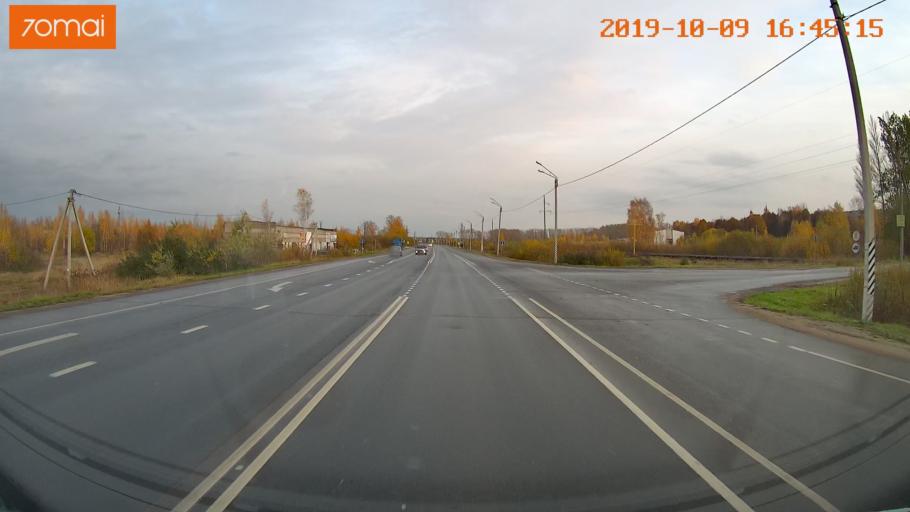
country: RU
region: Kostroma
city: Volgorechensk
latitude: 57.4473
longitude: 41.1520
